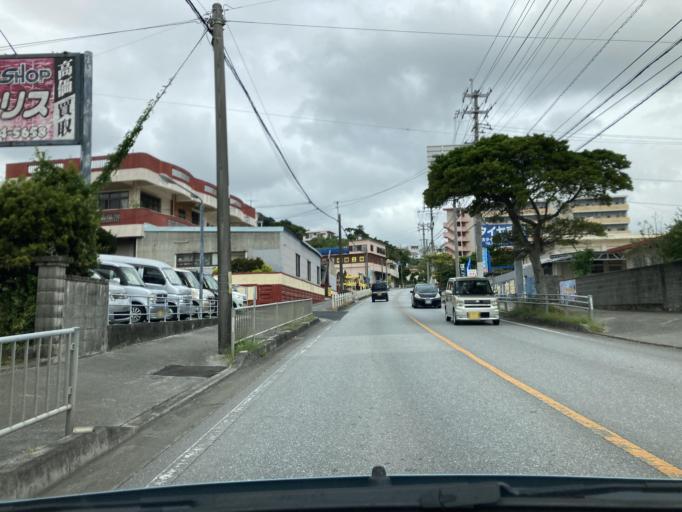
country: JP
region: Okinawa
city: Ginowan
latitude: 26.2323
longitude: 127.7527
